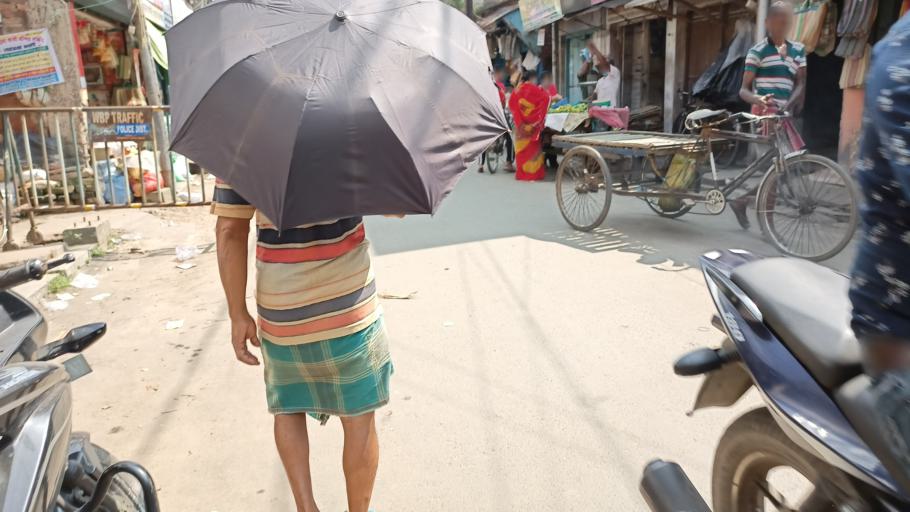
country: IN
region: West Bengal
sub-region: North 24 Parganas
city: Bangaon
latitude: 23.0453
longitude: 88.8309
